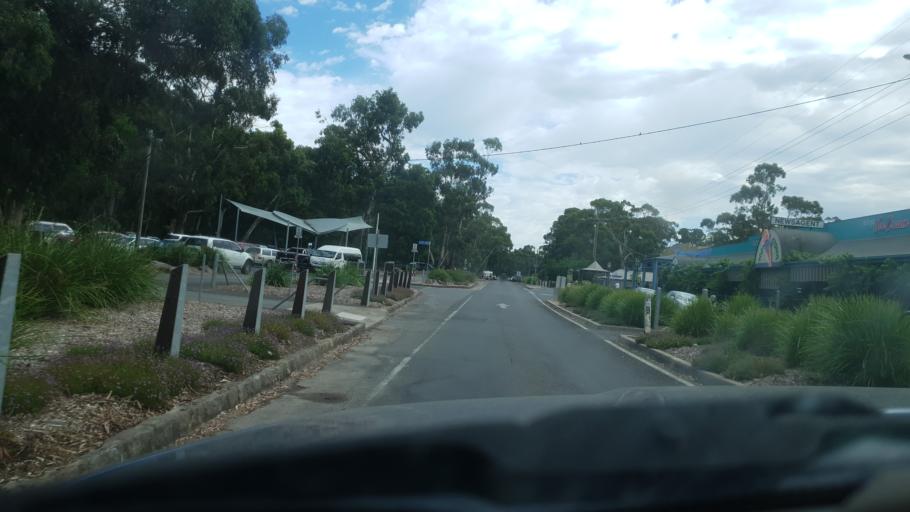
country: AU
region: Victoria
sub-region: Northern Grampians
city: Stawell
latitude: -37.1401
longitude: 142.5190
